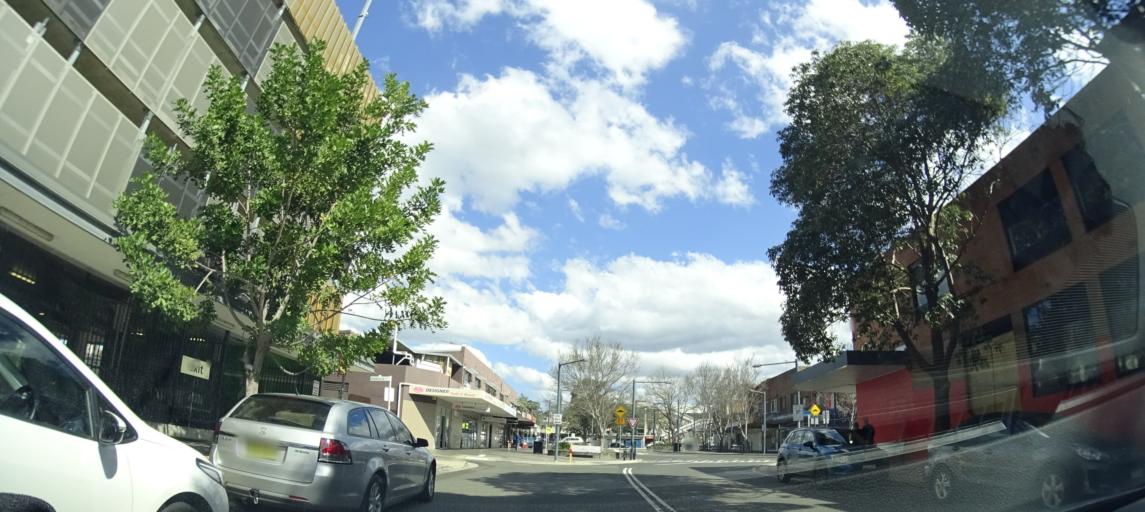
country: AU
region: New South Wales
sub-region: Bankstown
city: Revesby
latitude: -33.9510
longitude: 151.0158
